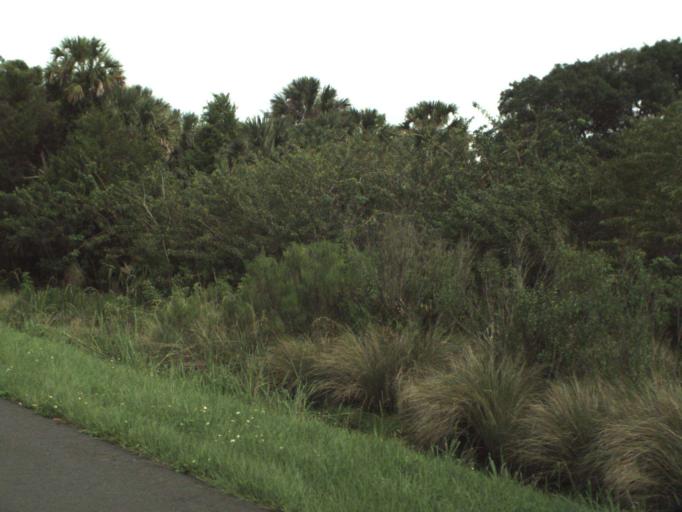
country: US
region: Florida
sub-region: Seminole County
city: Geneva
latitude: 28.7166
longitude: -81.0558
